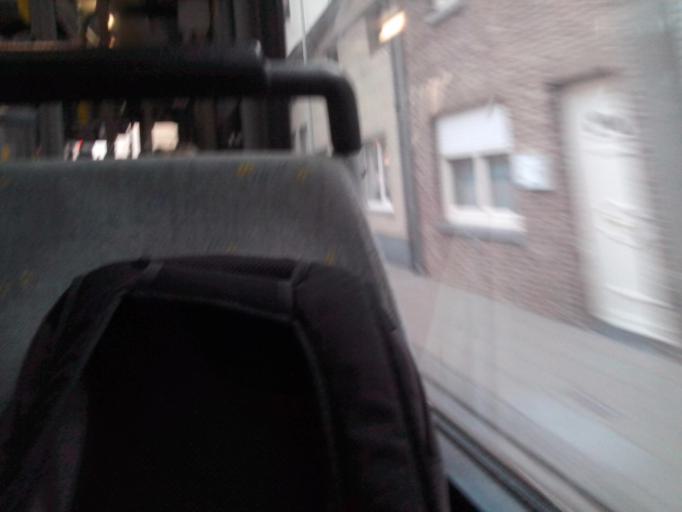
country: BE
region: Flanders
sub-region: Provincie Vlaams-Brabant
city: Asse
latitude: 50.9192
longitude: 4.1861
